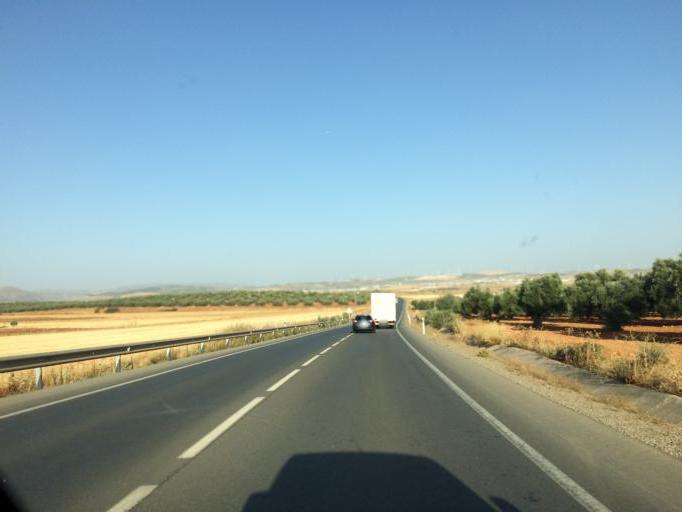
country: ES
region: Andalusia
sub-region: Provincia de Malaga
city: Campillos
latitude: 37.0498
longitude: -4.8185
